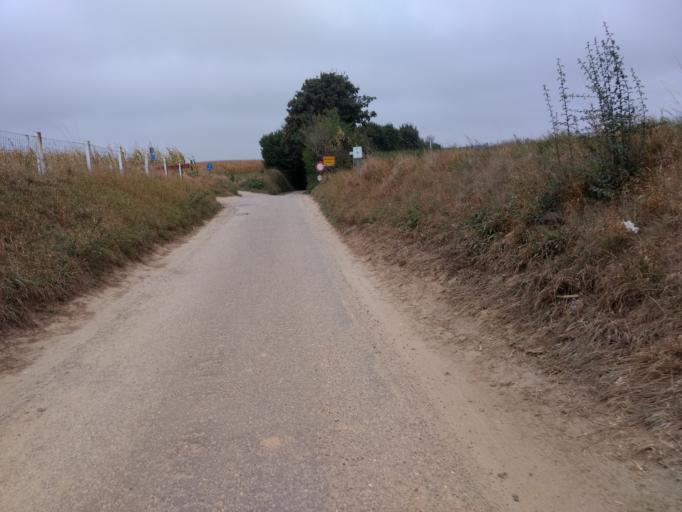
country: BE
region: Flanders
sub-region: Provincie Vlaams-Brabant
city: Herent
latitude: 50.8788
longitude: 4.6619
